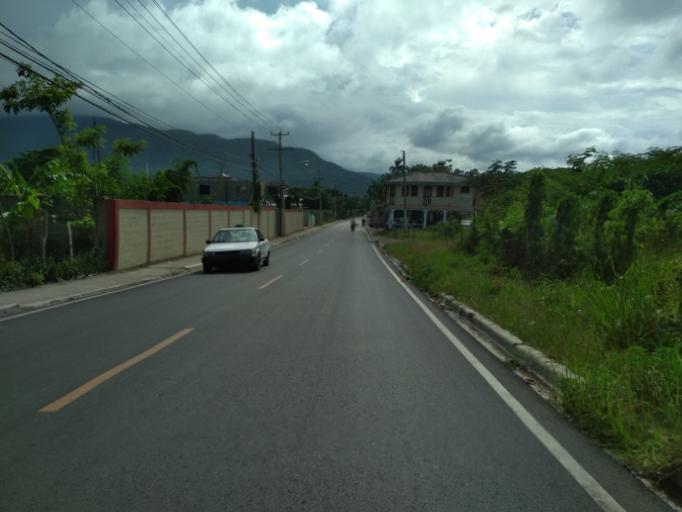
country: DO
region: Puerto Plata
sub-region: Puerto Plata
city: Puerto Plata
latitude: 19.8067
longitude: -70.7148
